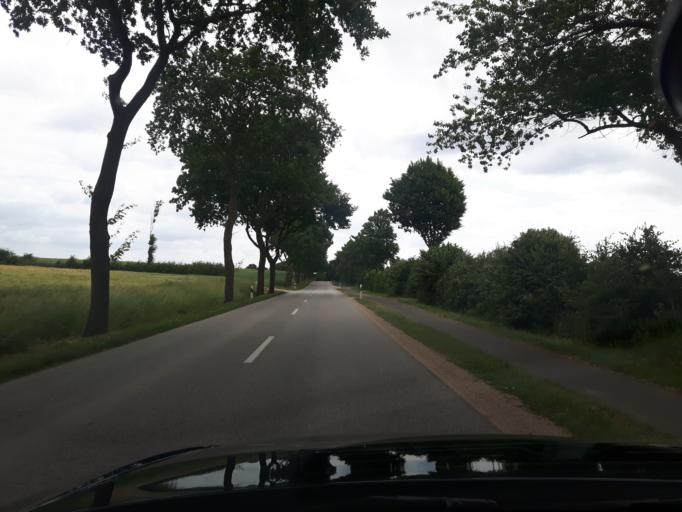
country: DE
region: Schleswig-Holstein
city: Neustadt in Holstein
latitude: 54.1020
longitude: 10.8438
